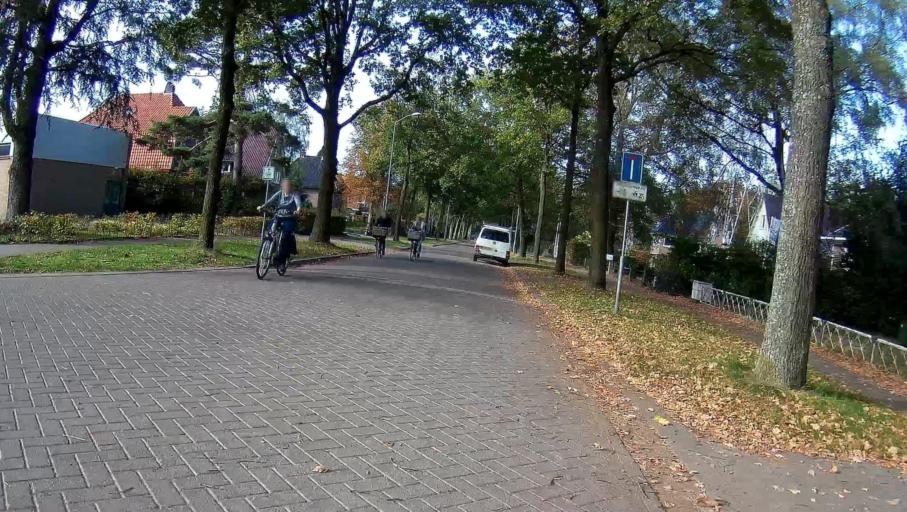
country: NL
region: Gelderland
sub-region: Gemeente Ede
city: Ede
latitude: 52.0502
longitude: 5.6628
